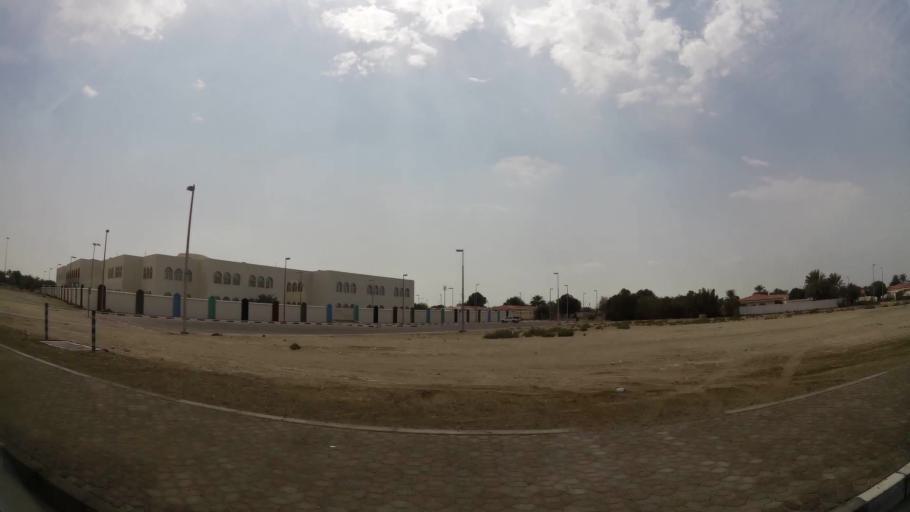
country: AE
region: Abu Dhabi
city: Abu Dhabi
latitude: 24.5228
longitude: 54.6881
